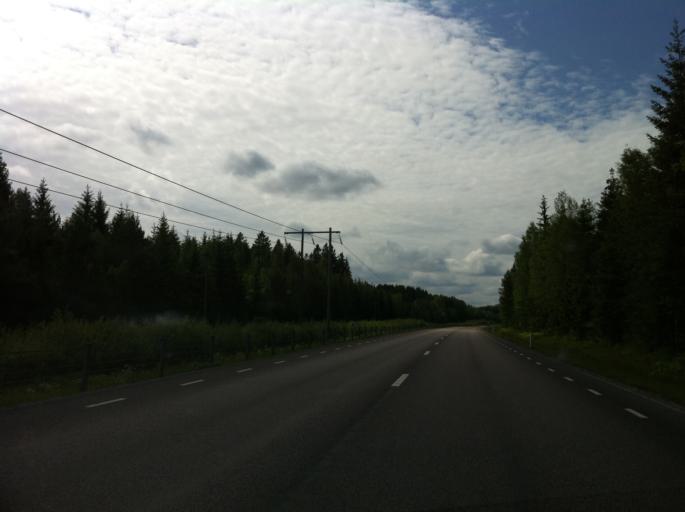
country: SE
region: Vaermland
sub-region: Karlstads Kommun
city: Edsvalla
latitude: 59.4348
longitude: 13.2009
